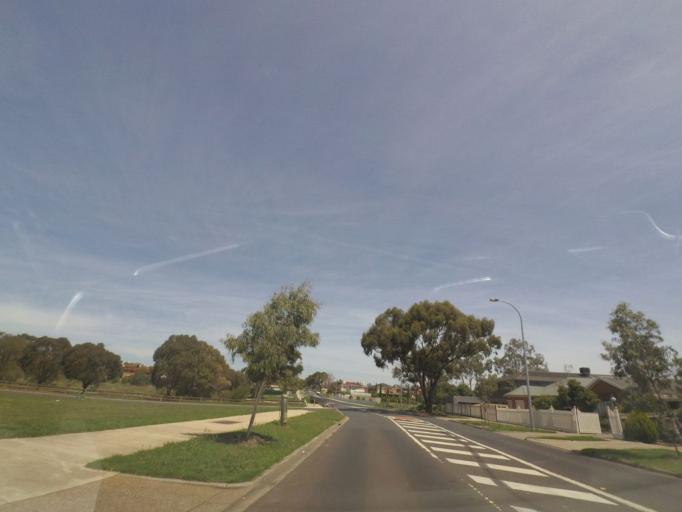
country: AU
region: Victoria
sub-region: Brimbank
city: Taylors Lakes
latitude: -37.6994
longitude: 144.7862
